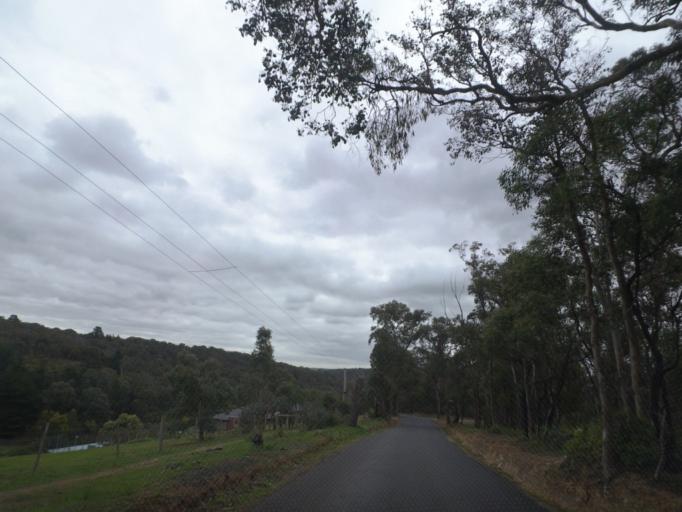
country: AU
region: Victoria
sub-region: Nillumbik
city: Hurstbridge
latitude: -37.6427
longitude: 145.2059
